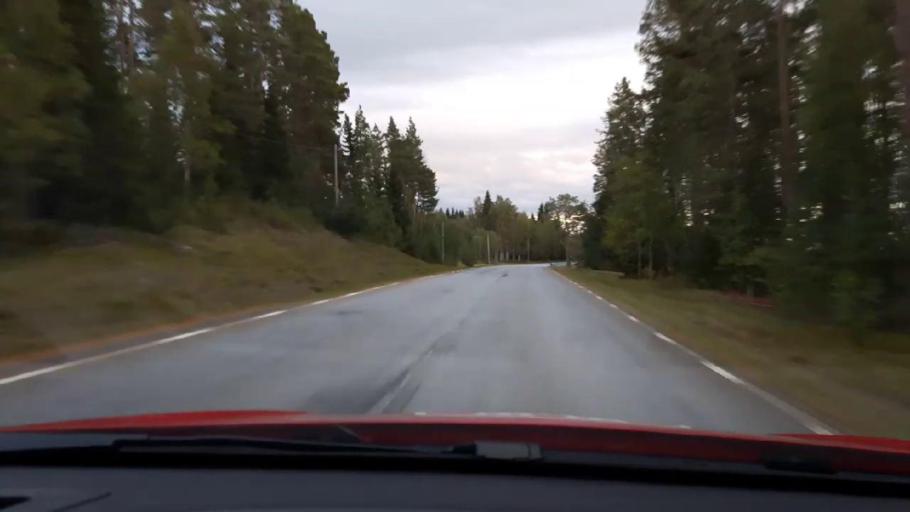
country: SE
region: Jaemtland
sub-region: Bergs Kommun
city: Hoverberg
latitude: 62.9955
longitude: 14.4828
